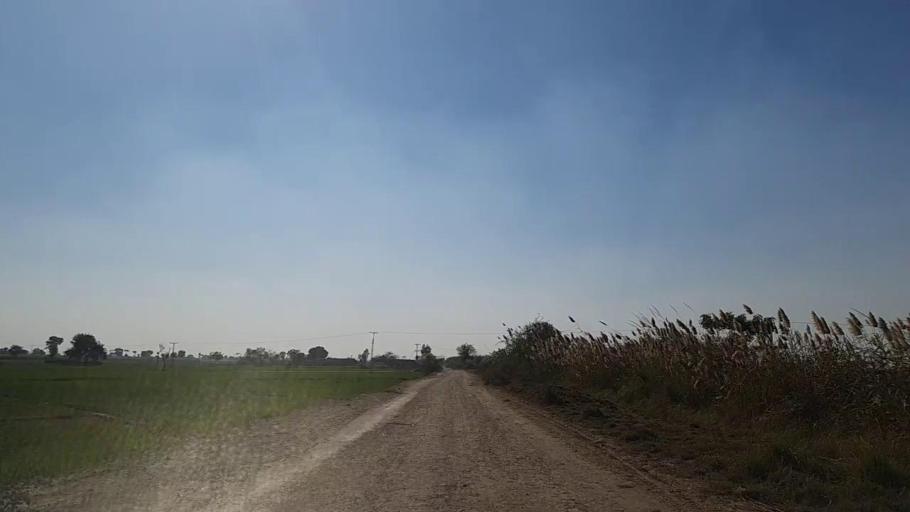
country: PK
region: Sindh
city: Bandhi
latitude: 26.5215
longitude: 68.2865
